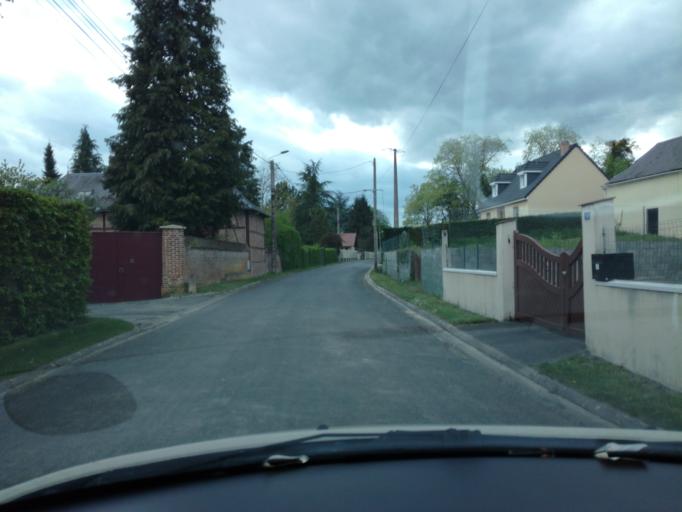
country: FR
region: Picardie
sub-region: Departement de la Somme
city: Quevauvillers
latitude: 49.8347
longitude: 2.0496
